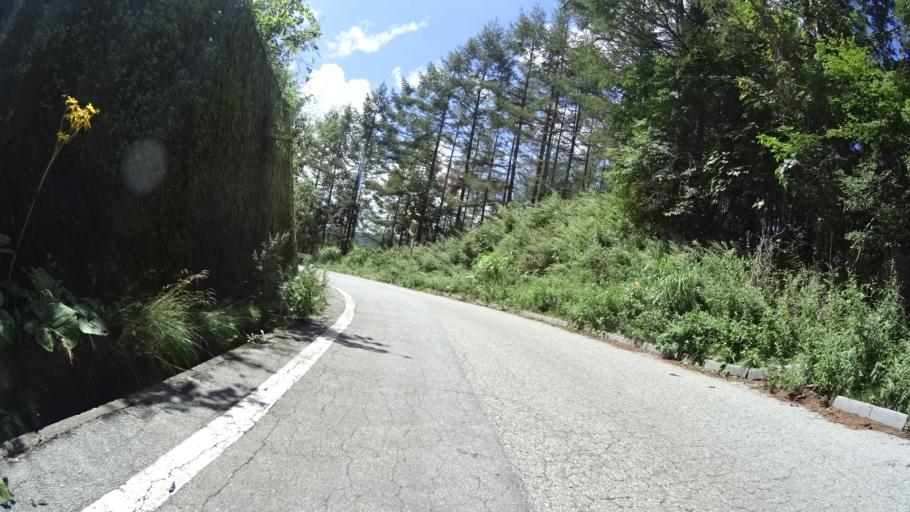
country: JP
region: Yamanashi
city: Enzan
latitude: 35.7180
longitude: 138.8386
